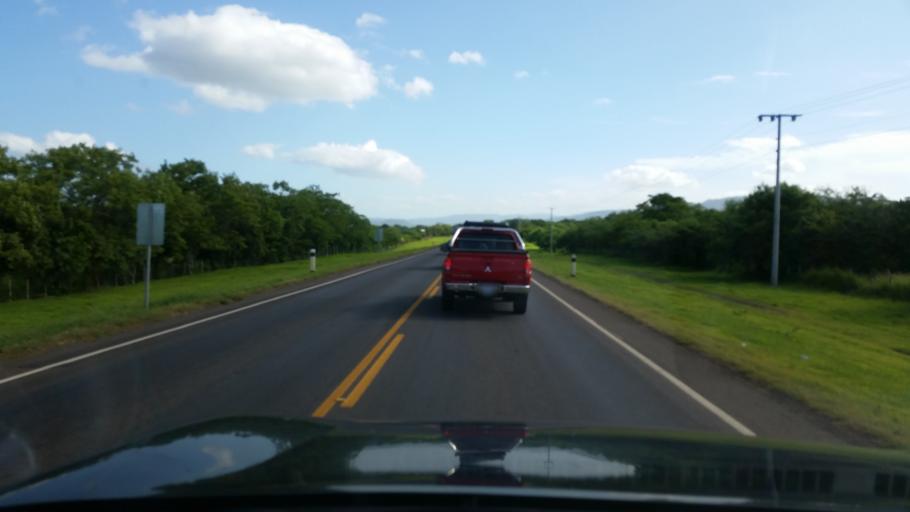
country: NI
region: Managua
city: Tipitapa
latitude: 12.3435
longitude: -86.0504
